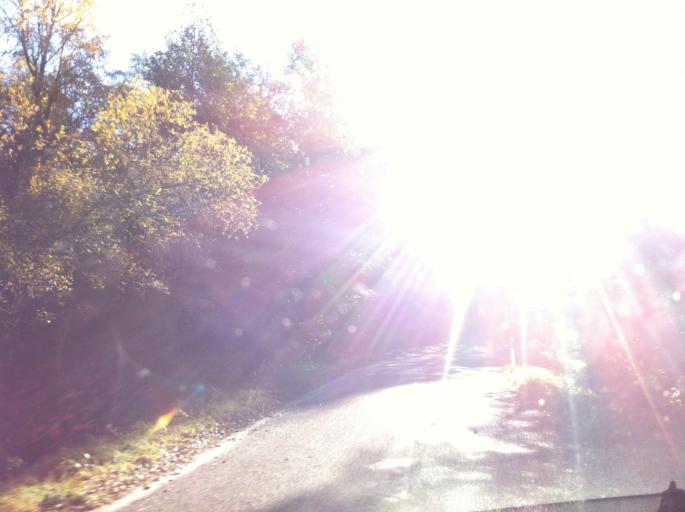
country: SE
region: Gaevleborg
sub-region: Gavle Kommun
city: Hedesunda
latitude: 60.3068
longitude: 17.0370
